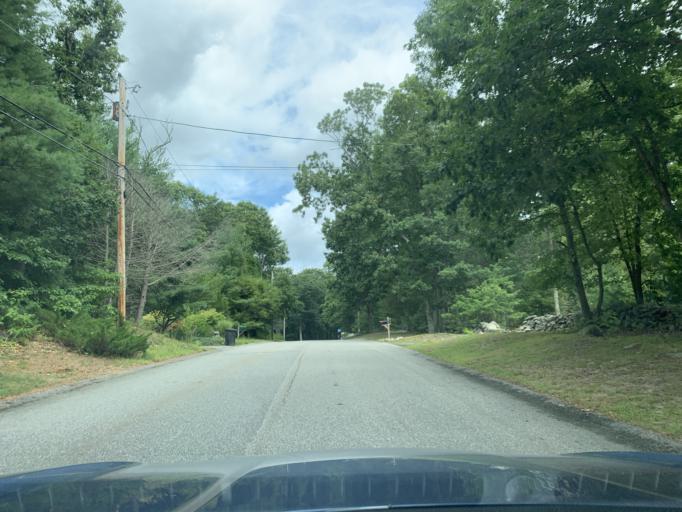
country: US
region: Rhode Island
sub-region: Kent County
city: West Warwick
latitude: 41.7391
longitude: -71.5947
